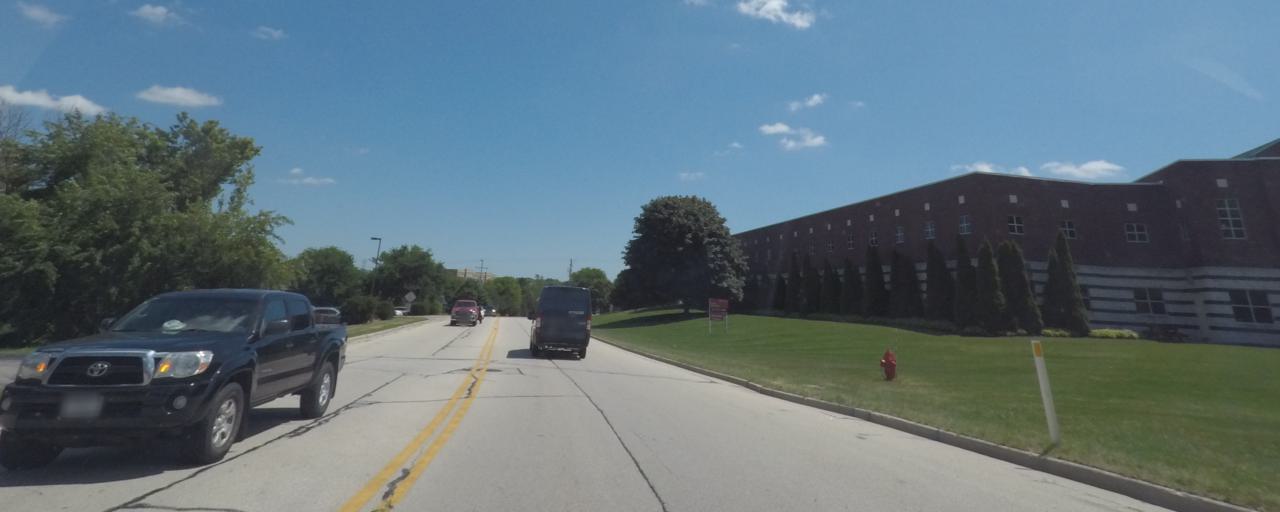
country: US
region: Wisconsin
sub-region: Waukesha County
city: Waukesha
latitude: 43.0383
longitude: -88.1708
